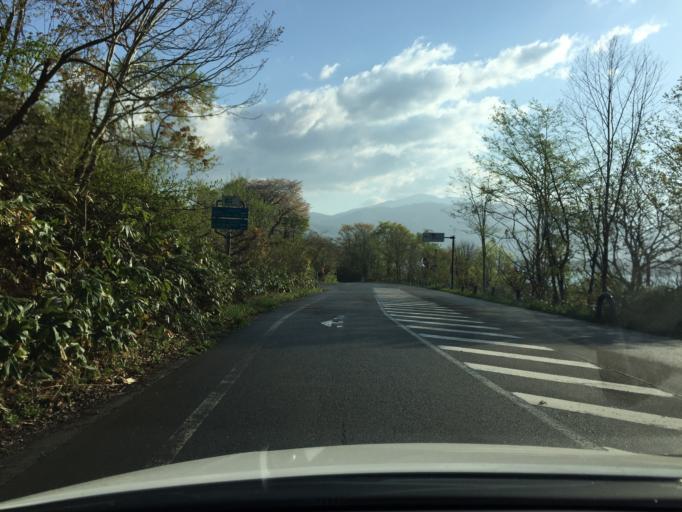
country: JP
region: Fukushima
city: Inawashiro
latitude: 37.6632
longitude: 140.0450
